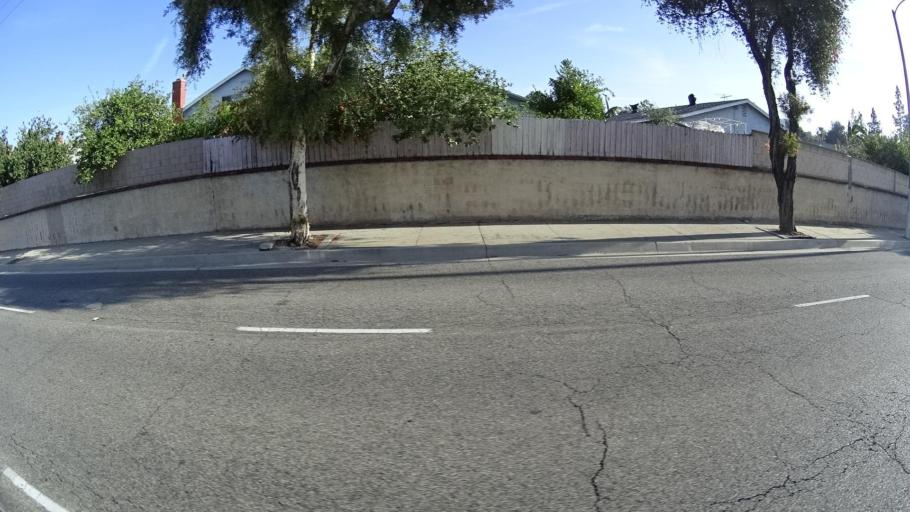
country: US
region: California
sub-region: Los Angeles County
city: Valinda
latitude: 34.0354
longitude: -117.9204
